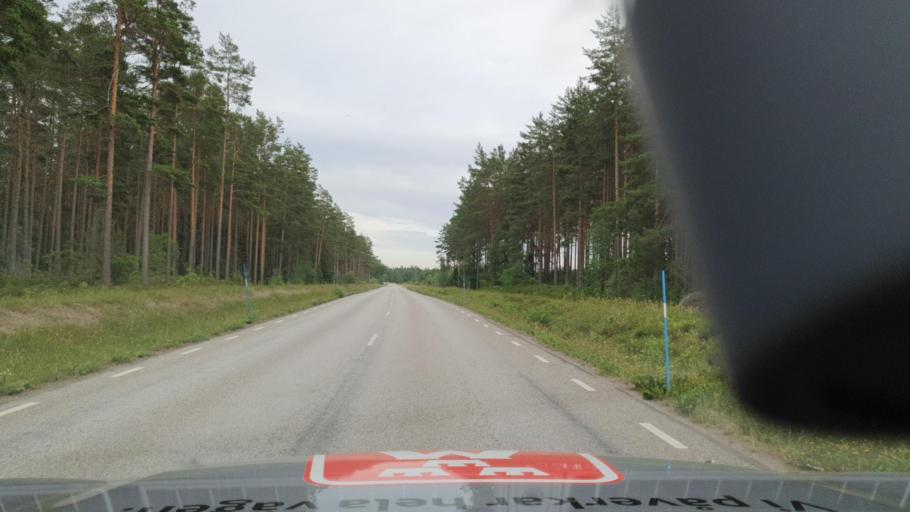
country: SE
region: Kalmar
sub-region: Nybro Kommun
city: Nybro
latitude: 56.6889
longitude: 15.9857
